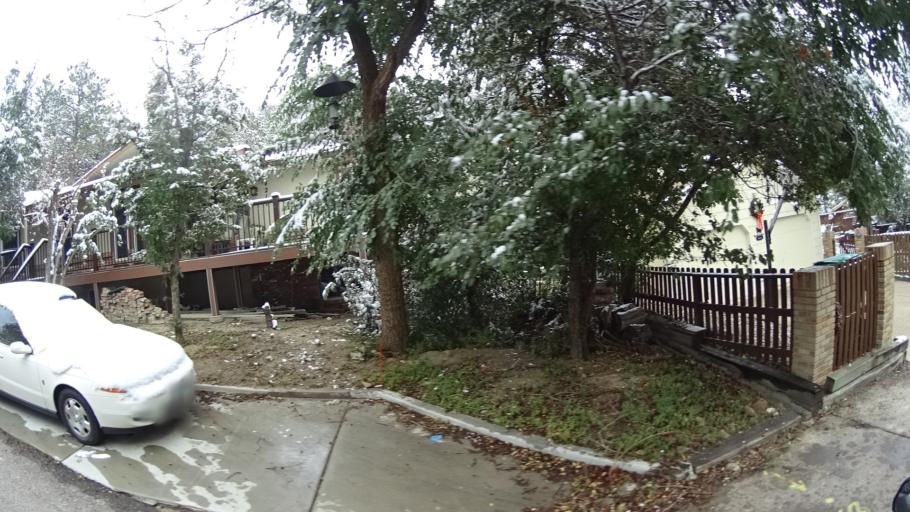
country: US
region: Colorado
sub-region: El Paso County
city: Colorado Springs
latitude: 38.8934
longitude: -104.7777
